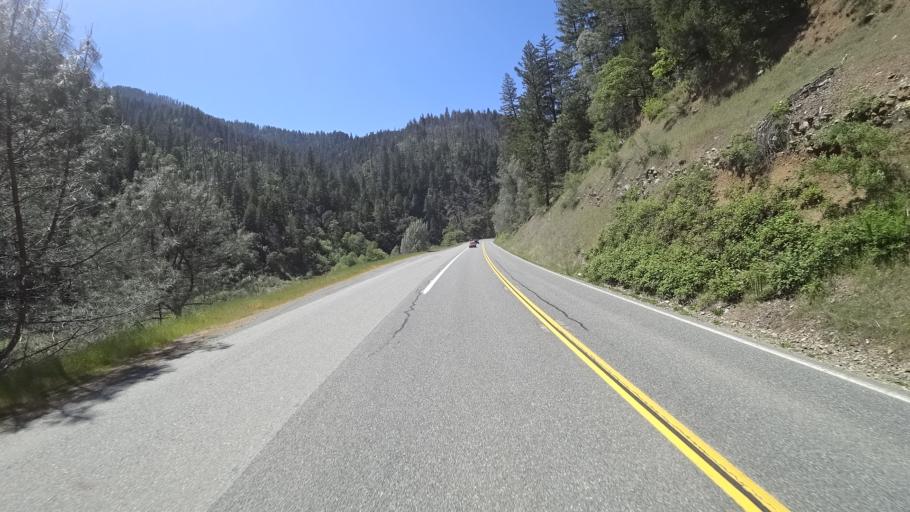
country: US
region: California
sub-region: Trinity County
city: Hayfork
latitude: 40.7661
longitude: -123.3029
